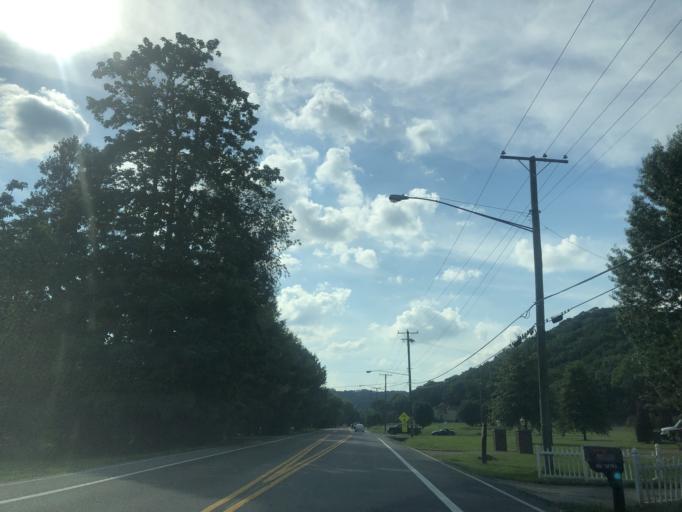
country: US
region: Tennessee
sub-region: Davidson County
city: Nashville
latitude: 36.2510
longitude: -86.8413
